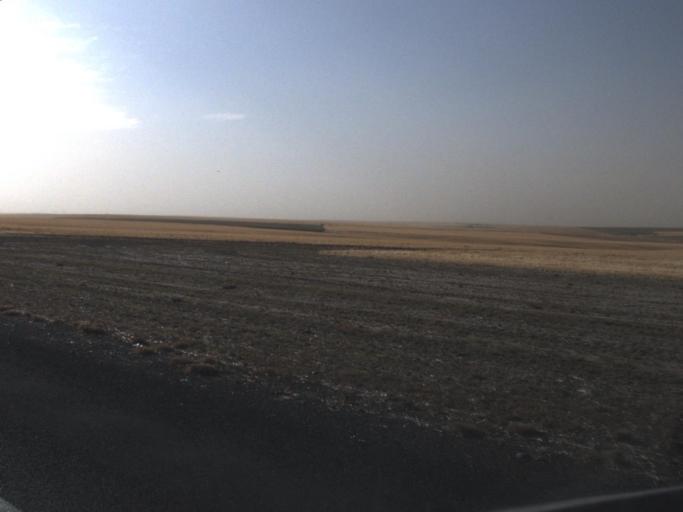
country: US
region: Washington
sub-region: Adams County
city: Ritzville
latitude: 47.3849
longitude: -118.4221
